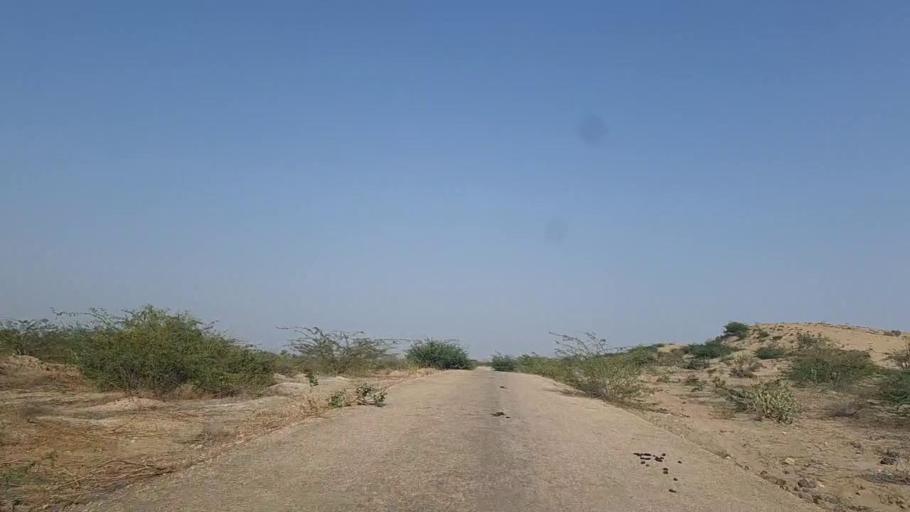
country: PK
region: Sindh
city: Naukot
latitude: 24.6284
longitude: 69.3604
